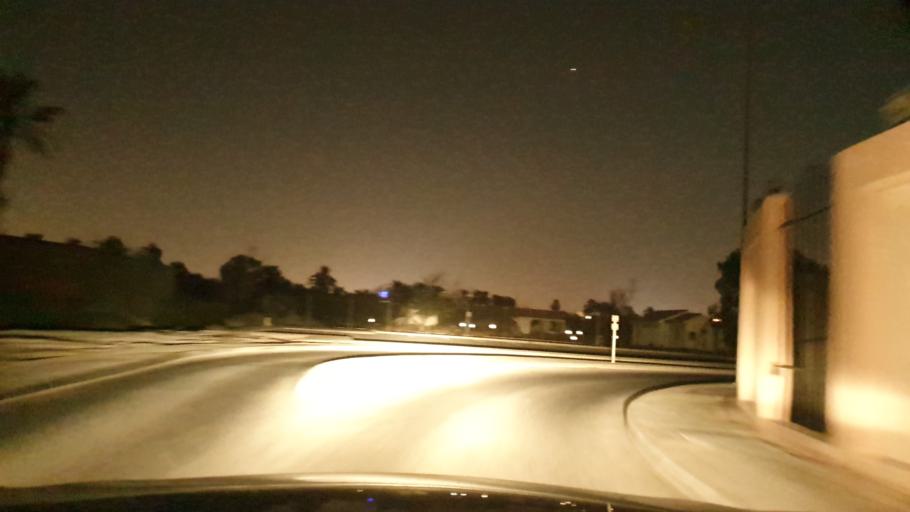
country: BH
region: Manama
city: Jidd Hafs
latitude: 26.1994
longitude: 50.5475
